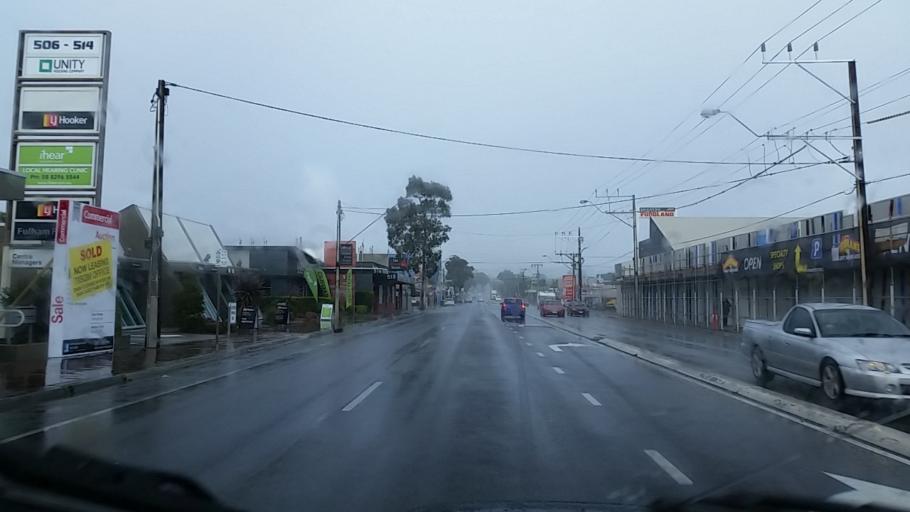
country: AU
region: South Australia
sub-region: Adelaide
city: Brighton
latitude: -35.0214
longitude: 138.5233
